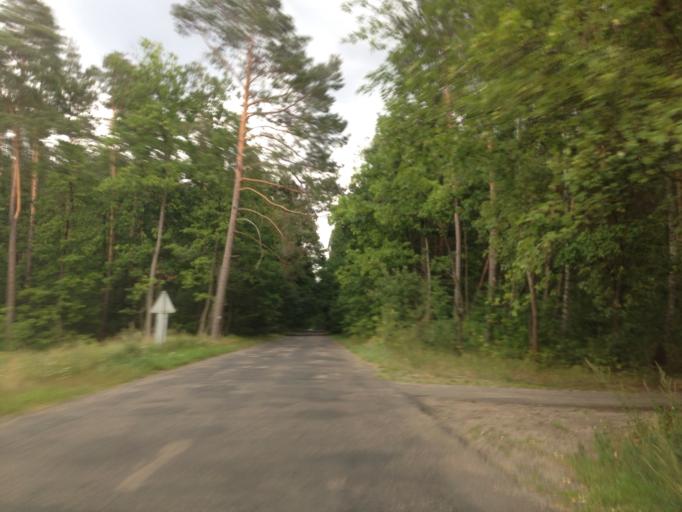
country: PL
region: Kujawsko-Pomorskie
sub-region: Powiat swiecki
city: Lniano
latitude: 53.5313
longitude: 18.1141
